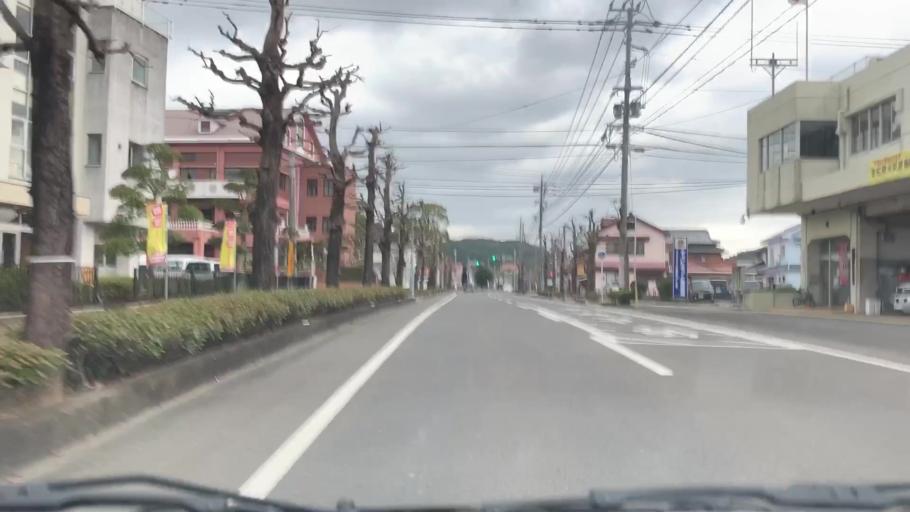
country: JP
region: Saga Prefecture
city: Ureshinomachi-shimojuku
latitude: 33.1011
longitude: 129.9874
